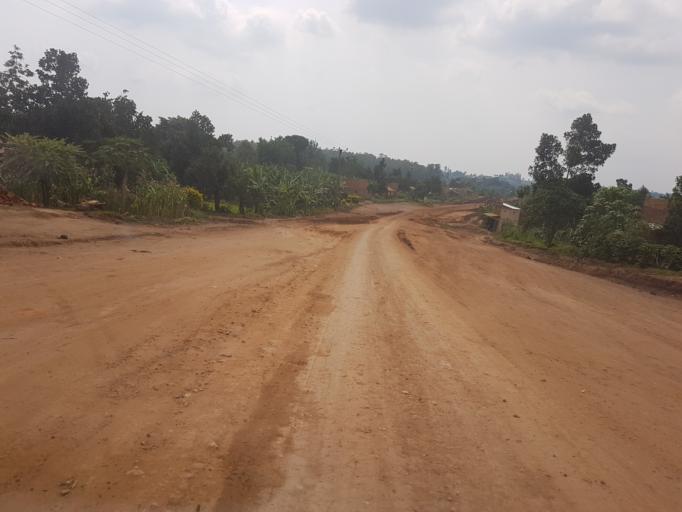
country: UG
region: Western Region
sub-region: Kanungu District
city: Ntungamo
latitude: -0.8047
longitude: 29.7037
